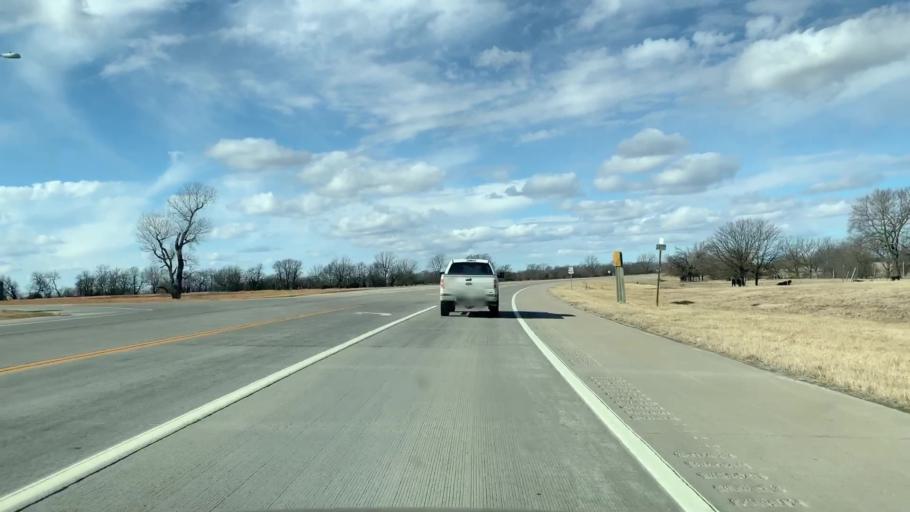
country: US
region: Kansas
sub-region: Labette County
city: Parsons
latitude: 37.3419
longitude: -95.1811
